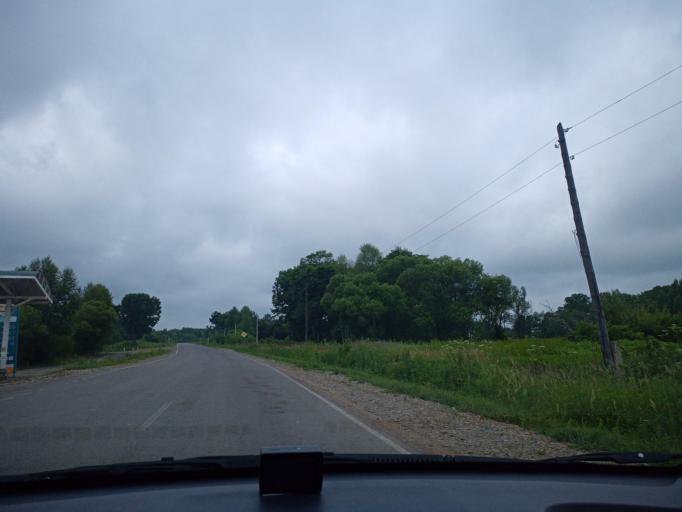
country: RU
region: Primorskiy
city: Novopokrovka
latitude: 45.8914
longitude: 134.8519
